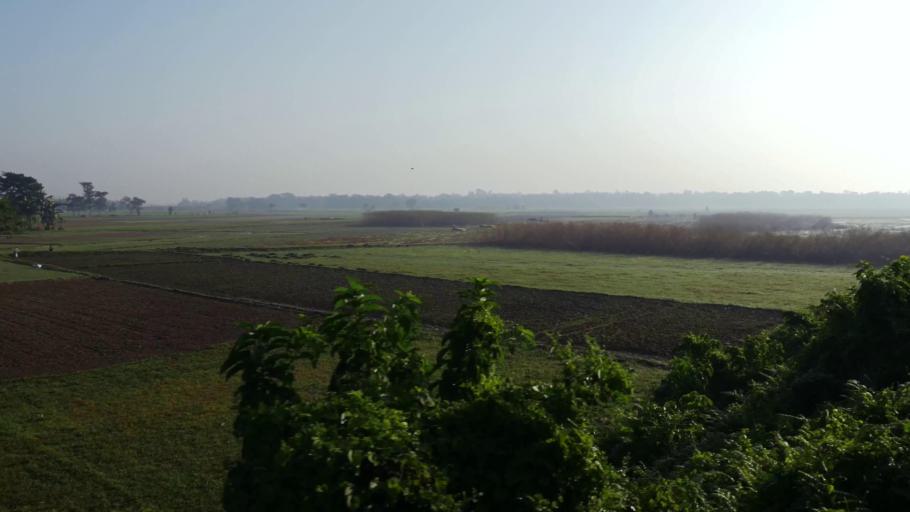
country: BD
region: Dhaka
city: Jamalpur
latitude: 24.9207
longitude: 89.9417
